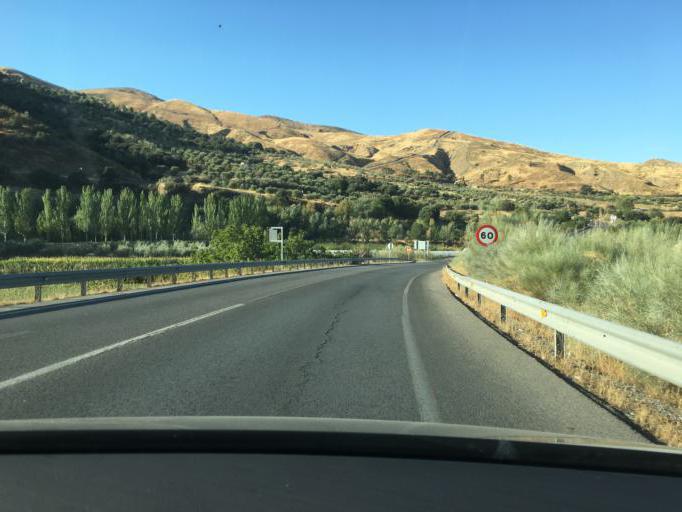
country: ES
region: Andalusia
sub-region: Provincia de Granada
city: Cenes de la Vega
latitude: 37.1571
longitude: -3.5300
